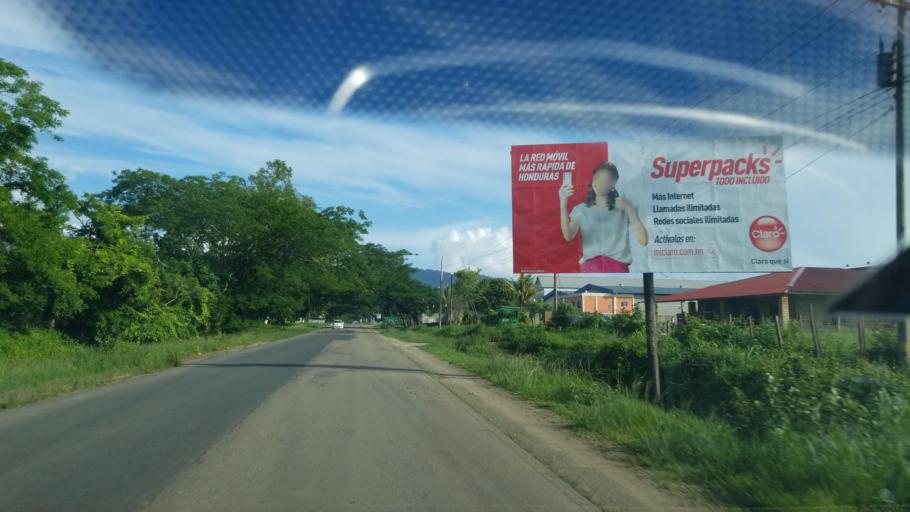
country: HN
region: El Paraiso
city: Cuyali
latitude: 13.8986
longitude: -86.5556
